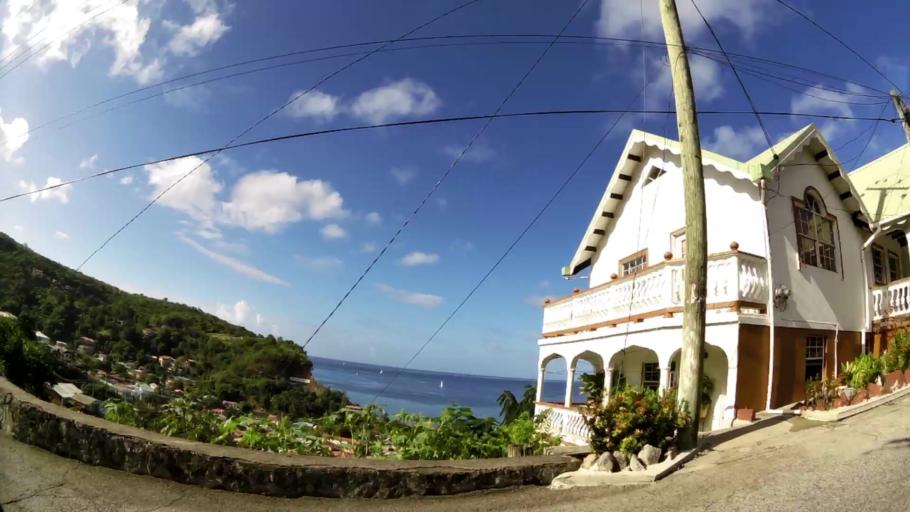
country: LC
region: Anse-la-Raye
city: Canaries
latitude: 13.9068
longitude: -61.0664
